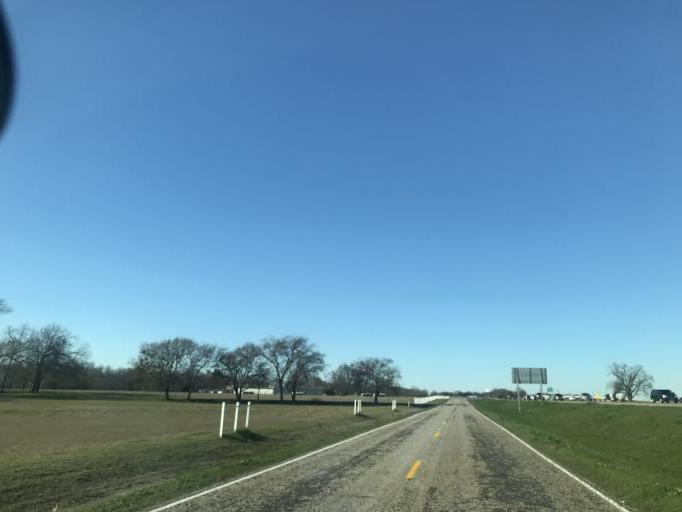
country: US
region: Texas
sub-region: Ellis County
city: Palmer
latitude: 32.4771
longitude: -96.6626
